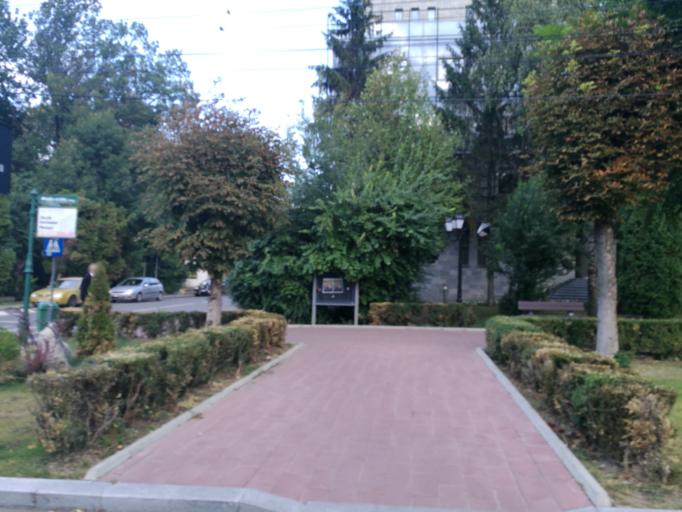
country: RO
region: Suceava
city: Suceava
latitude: 47.6424
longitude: 26.2585
